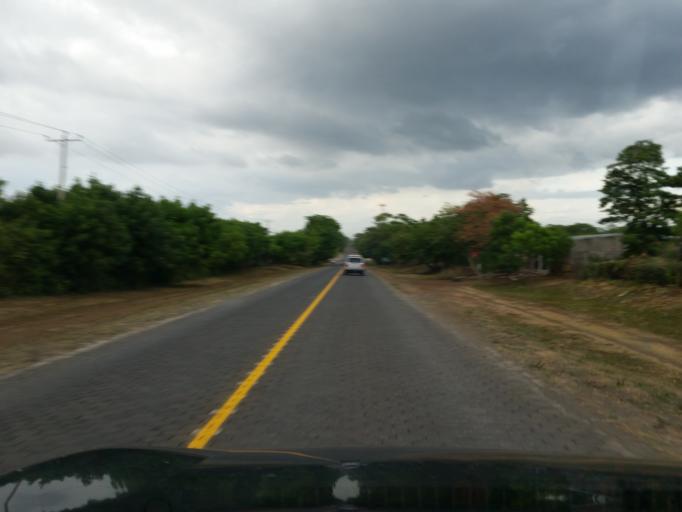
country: NI
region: Managua
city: Carlos Fonseca Amador
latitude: 11.9129
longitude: -86.5082
